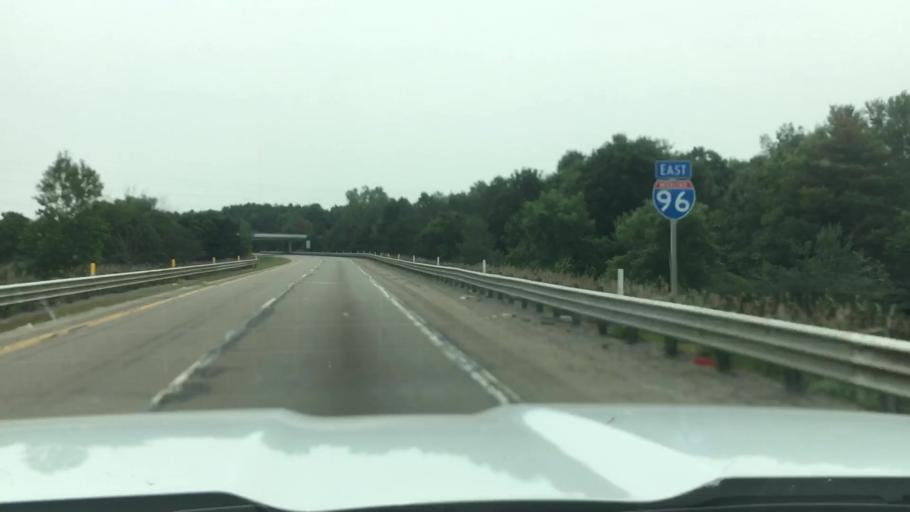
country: US
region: Michigan
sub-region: Eaton County
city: Dimondale
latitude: 42.6691
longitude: -84.6449
